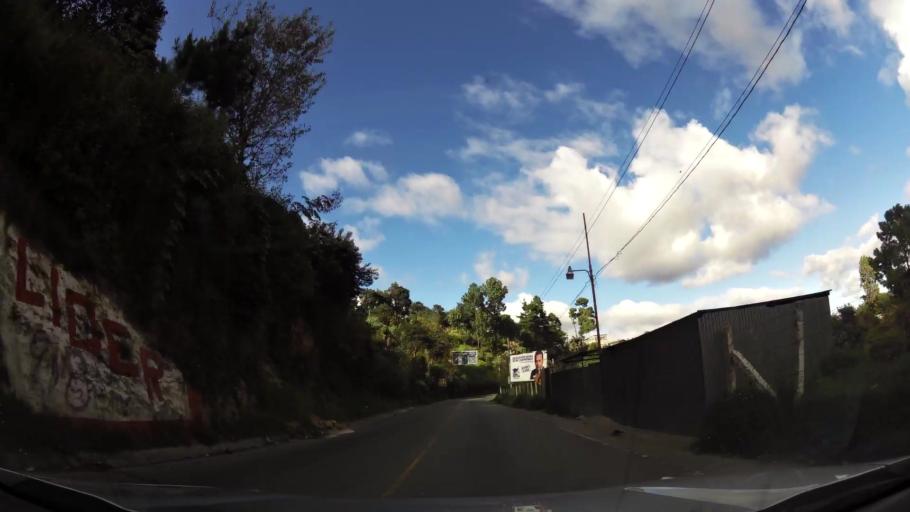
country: GT
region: Quiche
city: Chichicastenango
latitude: 14.9341
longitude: -91.1096
